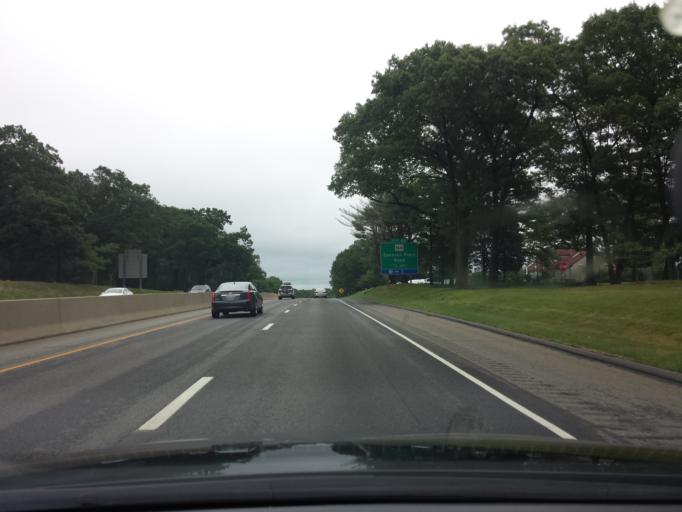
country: US
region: Connecticut
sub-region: Middlesex County
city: Westbrook Center
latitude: 41.2909
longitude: -72.4318
